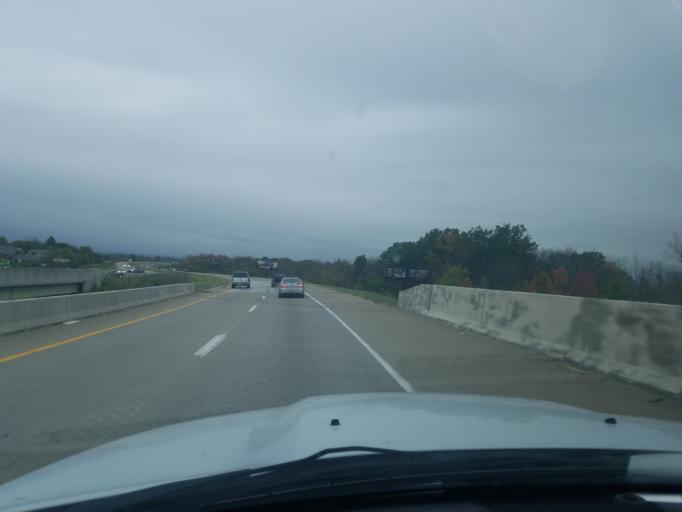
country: US
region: Indiana
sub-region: Clark County
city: Sellersburg
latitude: 38.3489
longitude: -85.7321
